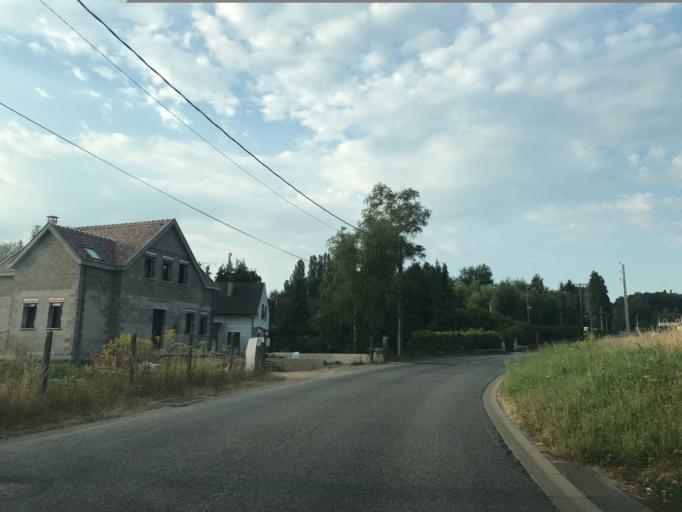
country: FR
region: Ile-de-France
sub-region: Departement des Yvelines
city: Jouars-Pontchartrain
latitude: 48.7620
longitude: 1.8847
